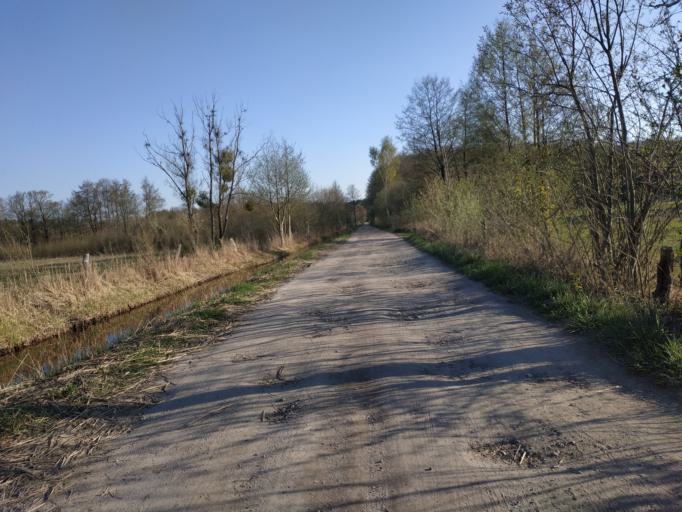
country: DE
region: Brandenburg
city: Strausberg
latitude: 52.5567
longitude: 13.8448
